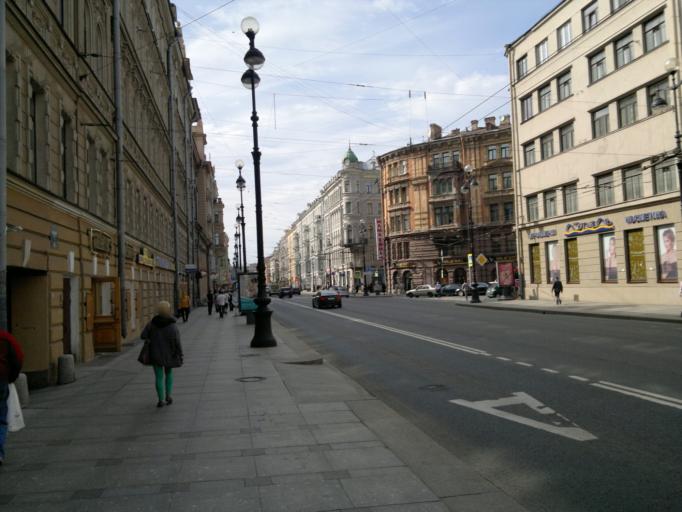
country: RU
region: St.-Petersburg
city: Centralniy
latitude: 59.9289
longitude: 30.3702
